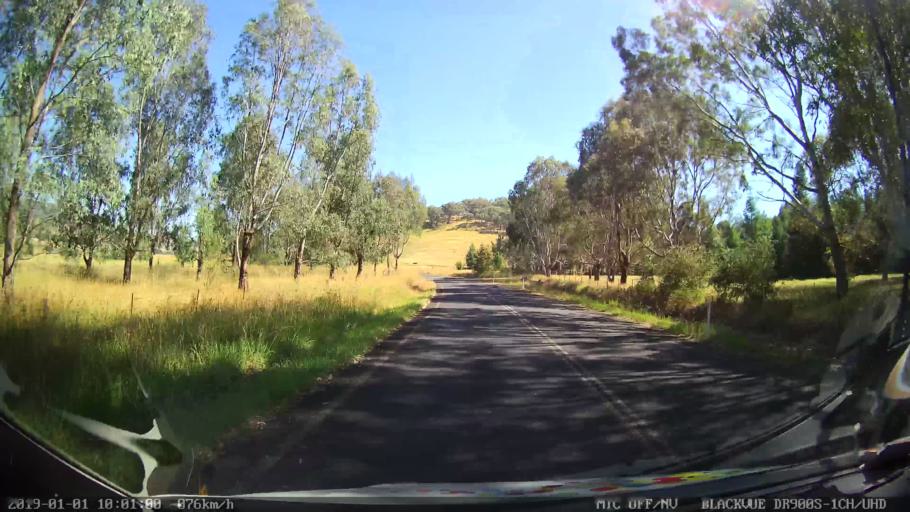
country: AU
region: New South Wales
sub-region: Snowy River
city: Jindabyne
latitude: -36.1960
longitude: 148.1031
